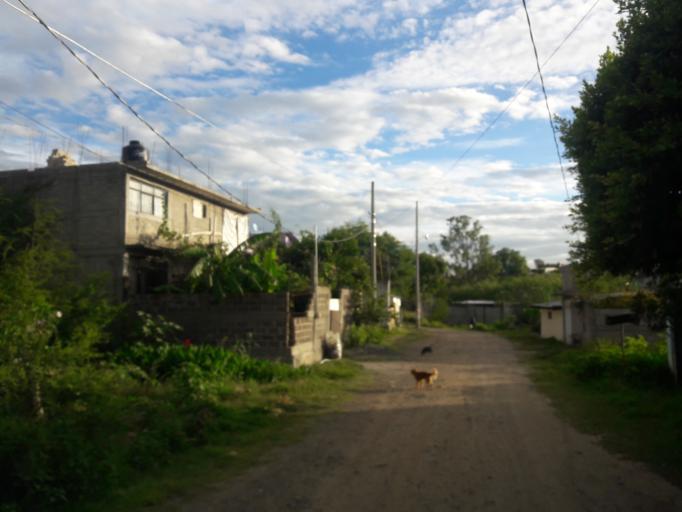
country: MX
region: Oaxaca
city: Ciudad de Huajuapam de Leon
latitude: 17.8034
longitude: -97.7851
